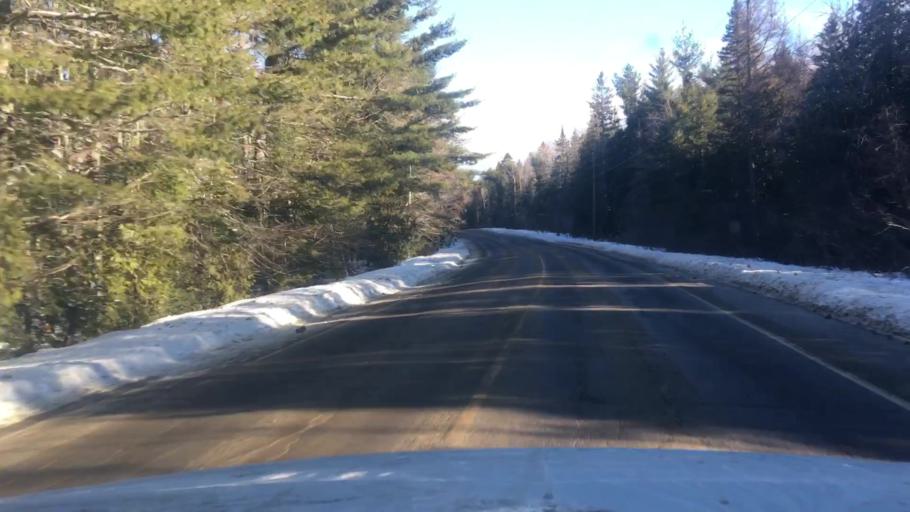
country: US
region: Maine
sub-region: Hancock County
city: Ellsworth
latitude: 44.6628
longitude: -68.3564
